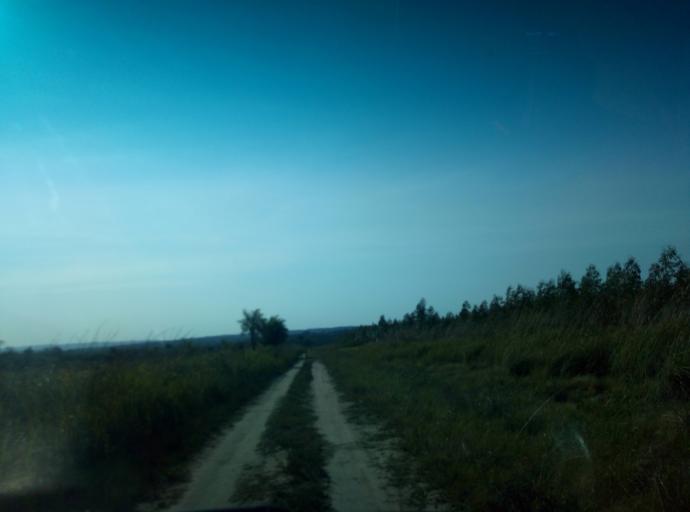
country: PY
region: Caaguazu
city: Doctor Cecilio Baez
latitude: -25.1910
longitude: -56.1961
